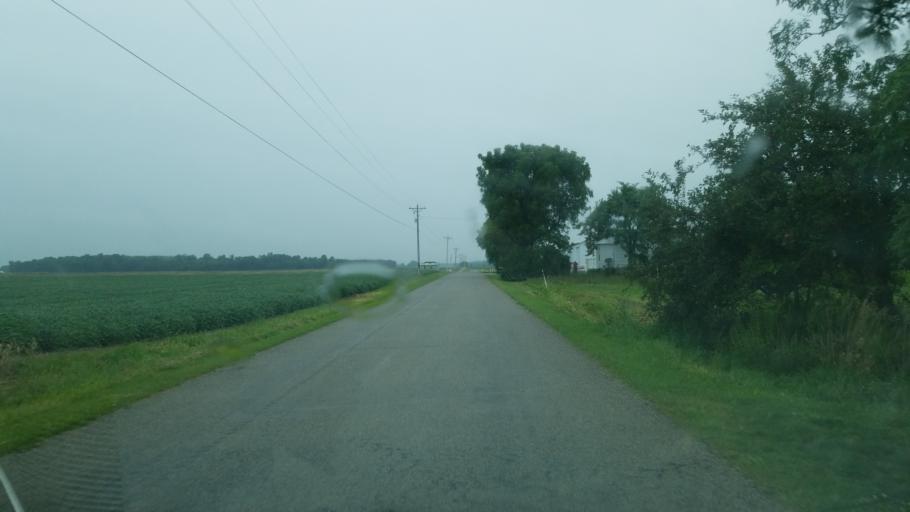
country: US
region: Ohio
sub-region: Huron County
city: Willard
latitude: 41.0052
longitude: -82.8139
